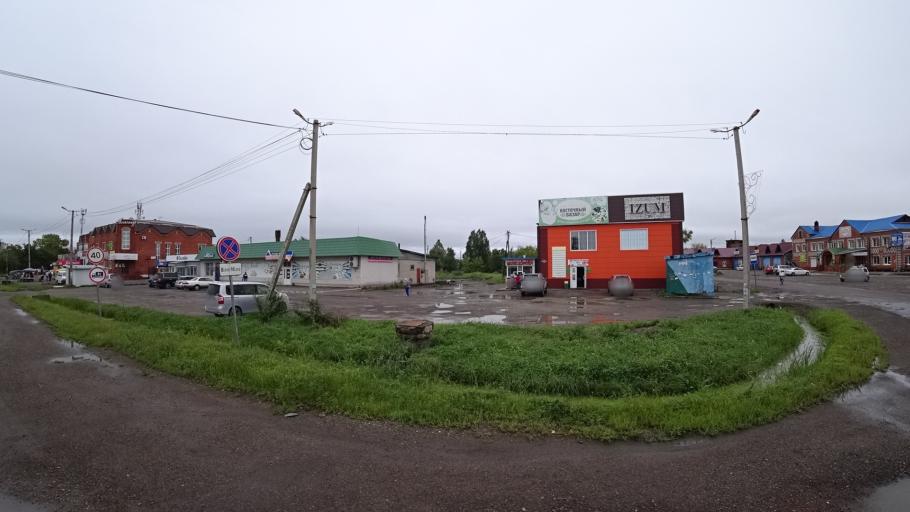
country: RU
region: Primorskiy
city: Monastyrishche
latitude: 44.2059
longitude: 132.4413
